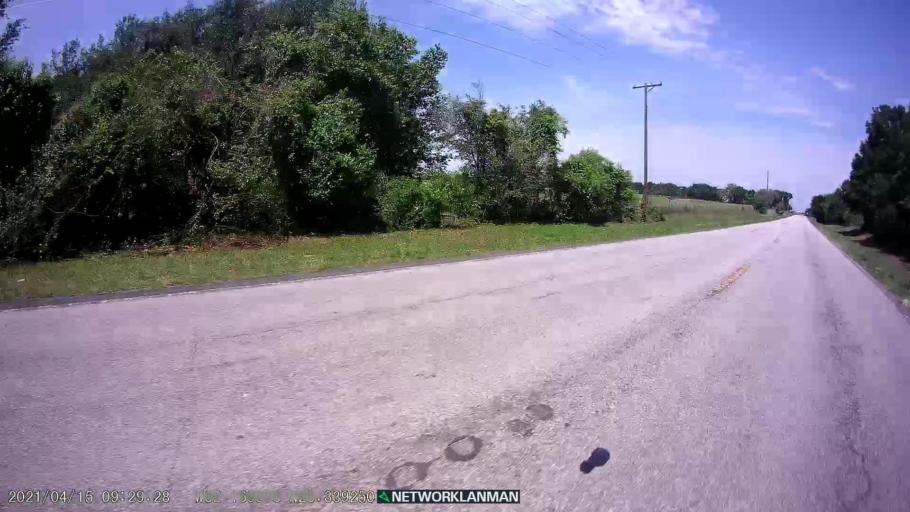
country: US
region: Florida
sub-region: Pasco County
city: Dade City
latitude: 28.3398
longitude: -82.1694
